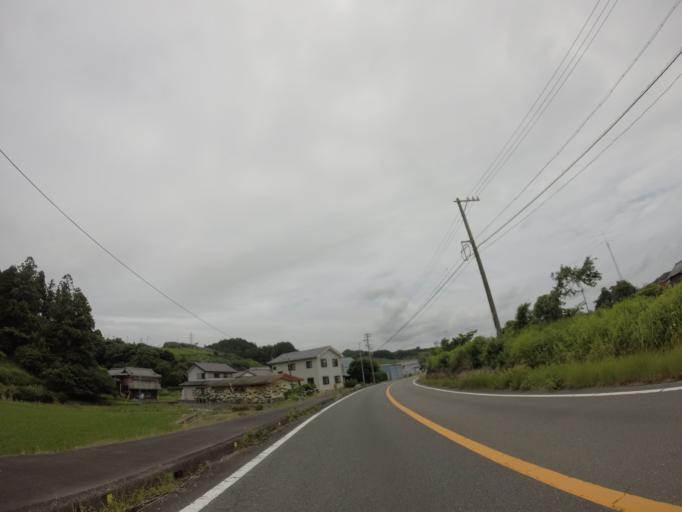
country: JP
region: Shizuoka
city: Shimada
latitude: 34.7801
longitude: 138.1672
